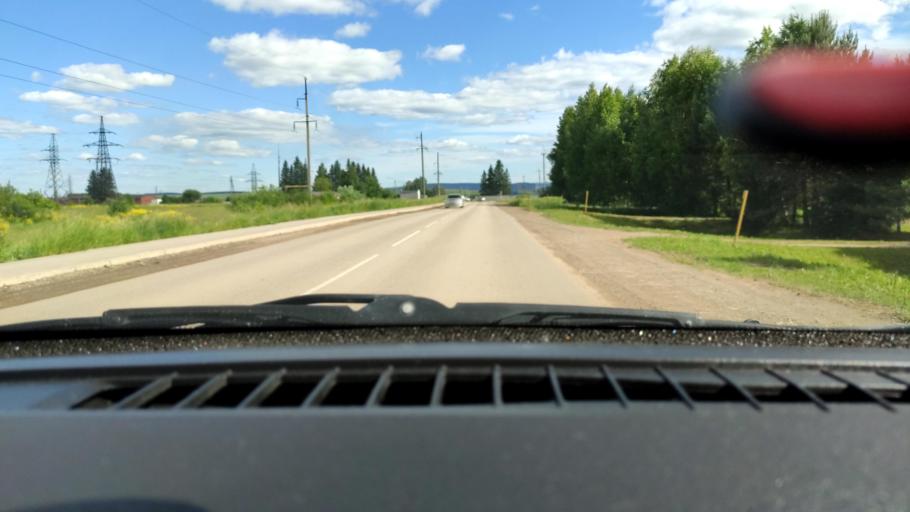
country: RU
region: Perm
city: Kultayevo
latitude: 57.8898
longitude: 55.9214
